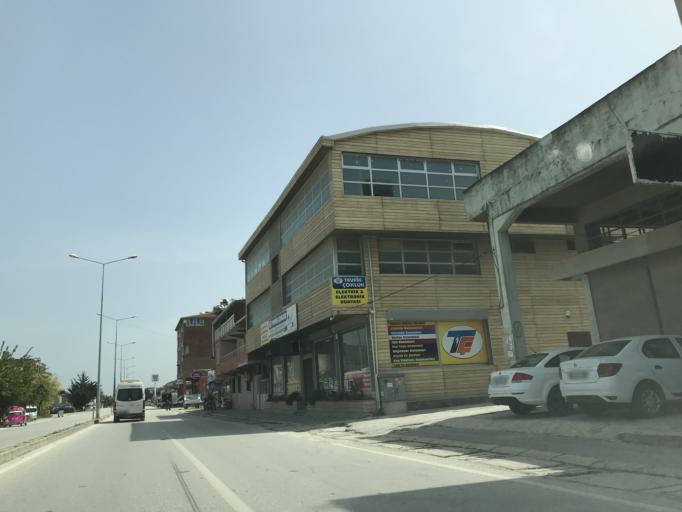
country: TR
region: Hatay
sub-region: Antakya Ilcesi
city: Antakya
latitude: 36.2141
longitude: 36.1786
